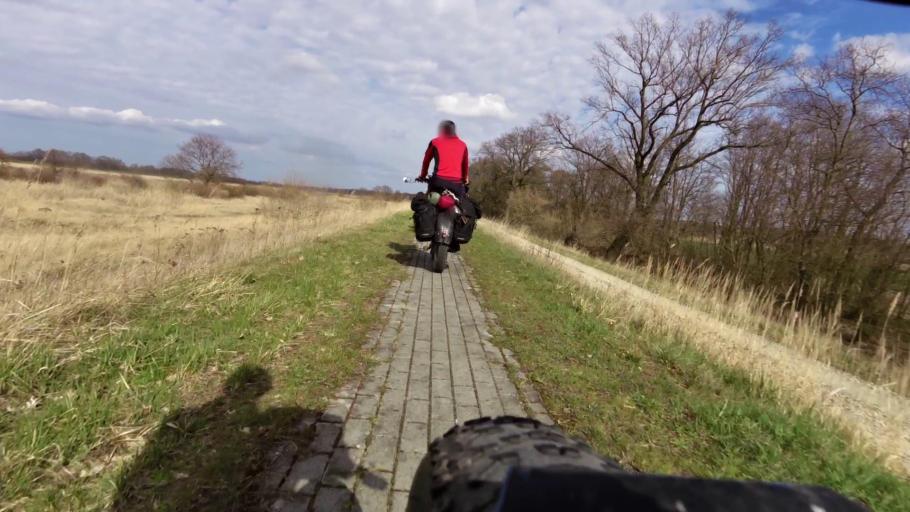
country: PL
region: Lubusz
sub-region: Powiat slubicki
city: Gorzyca
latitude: 52.4766
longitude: 14.6182
